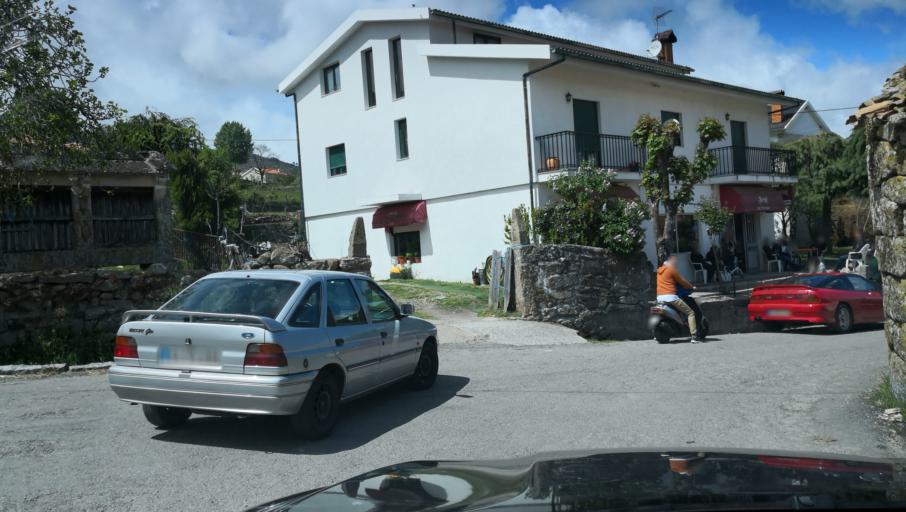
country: PT
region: Vila Real
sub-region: Vila Real
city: Vila Real
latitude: 41.4070
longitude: -7.7151
